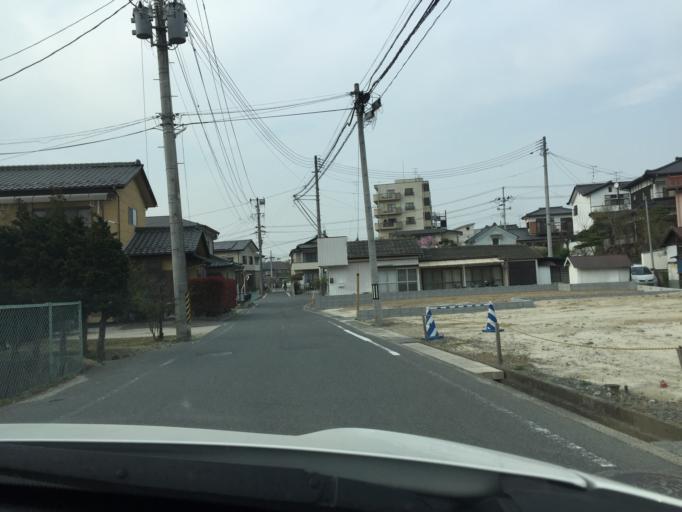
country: JP
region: Fukushima
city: Iwaki
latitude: 37.0601
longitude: 140.8773
